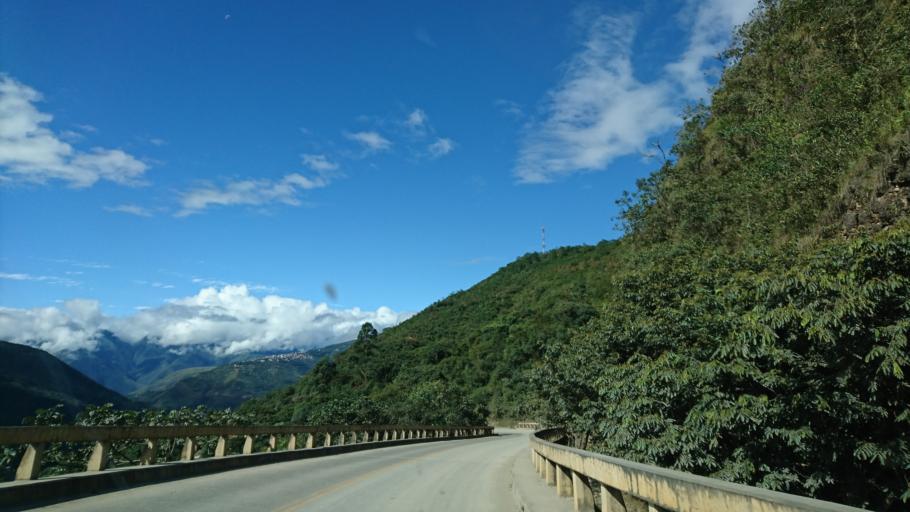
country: BO
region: La Paz
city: Coroico
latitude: -16.2086
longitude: -67.7876
